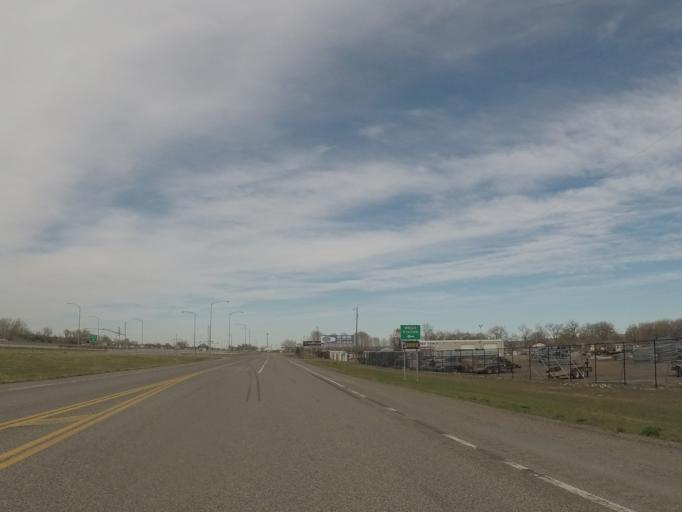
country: US
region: Montana
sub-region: Yellowstone County
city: Laurel
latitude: 45.6901
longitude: -108.6882
